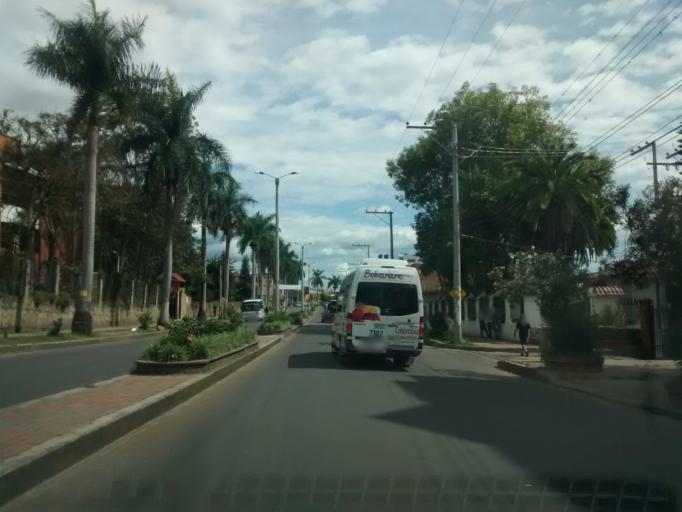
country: CO
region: Cundinamarca
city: Fusagasuga
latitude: 4.3381
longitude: -74.3647
